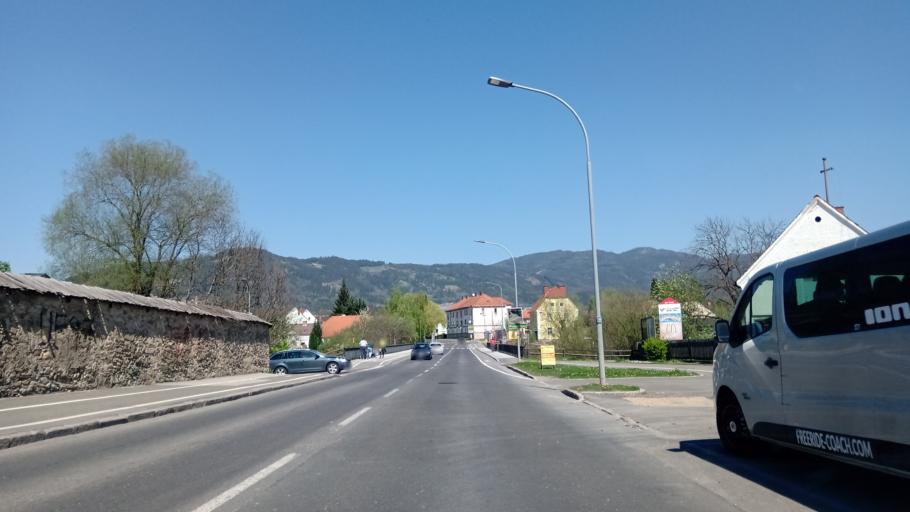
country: AT
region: Styria
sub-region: Politischer Bezirk Leoben
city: Leoben
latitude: 47.3647
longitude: 15.0952
